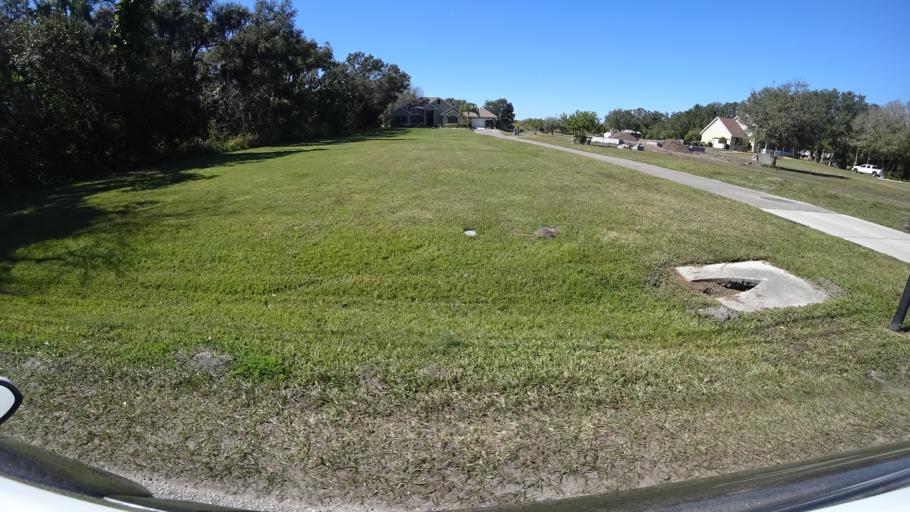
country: US
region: Florida
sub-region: Manatee County
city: Memphis
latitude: 27.5617
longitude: -82.5483
